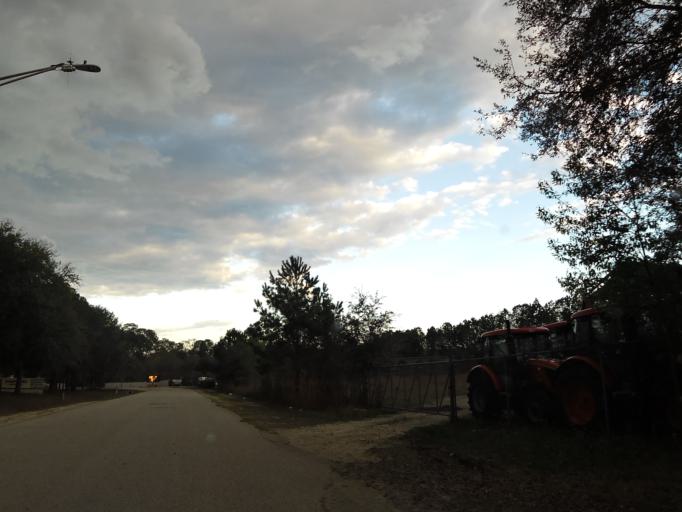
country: US
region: Florida
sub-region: Saint Johns County
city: Fruit Cove
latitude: 30.1843
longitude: -81.5668
